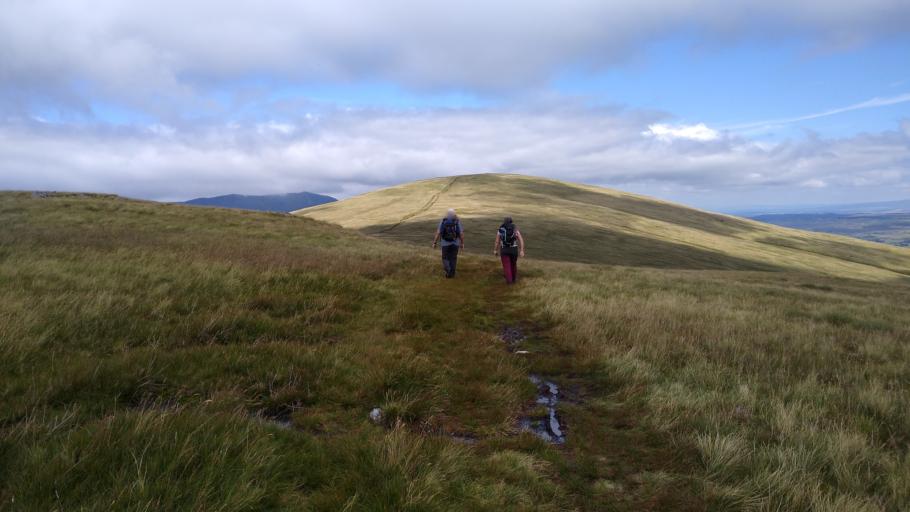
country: GB
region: England
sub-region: Cumbria
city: Keswick
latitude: 54.5803
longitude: -3.0349
